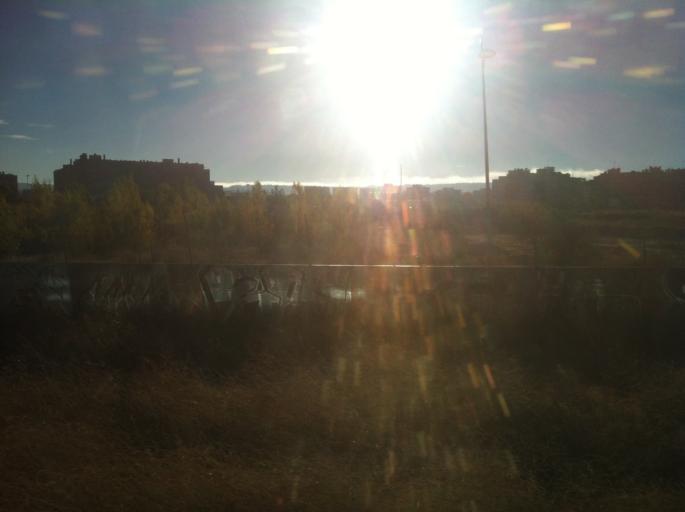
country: ES
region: Castille and Leon
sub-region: Provincia de Valladolid
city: Valladolid
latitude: 41.6576
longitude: -4.7057
